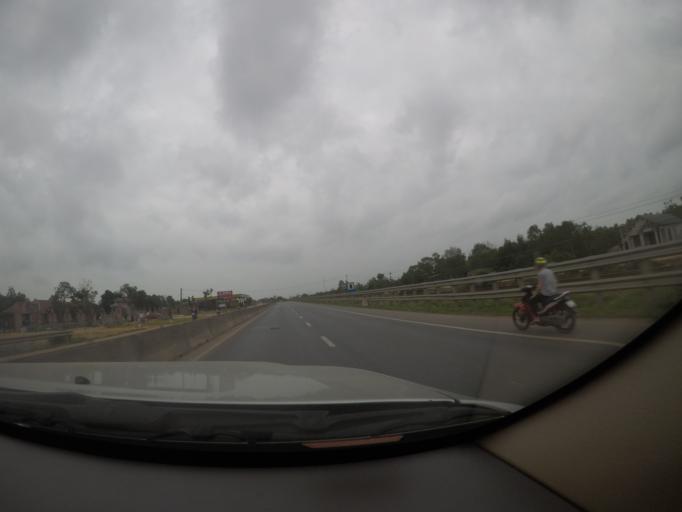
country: VN
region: Quang Tri
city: Hai Lang
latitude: 16.7101
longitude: 107.2176
